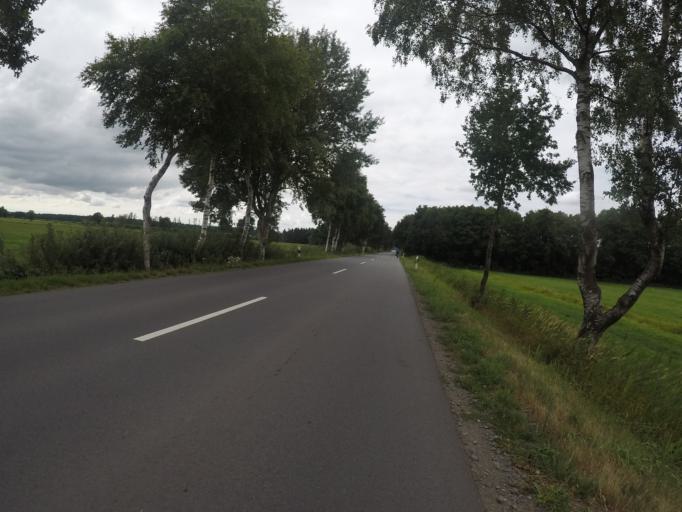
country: DE
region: Lower Saxony
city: Wingst
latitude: 53.7059
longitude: 9.0724
